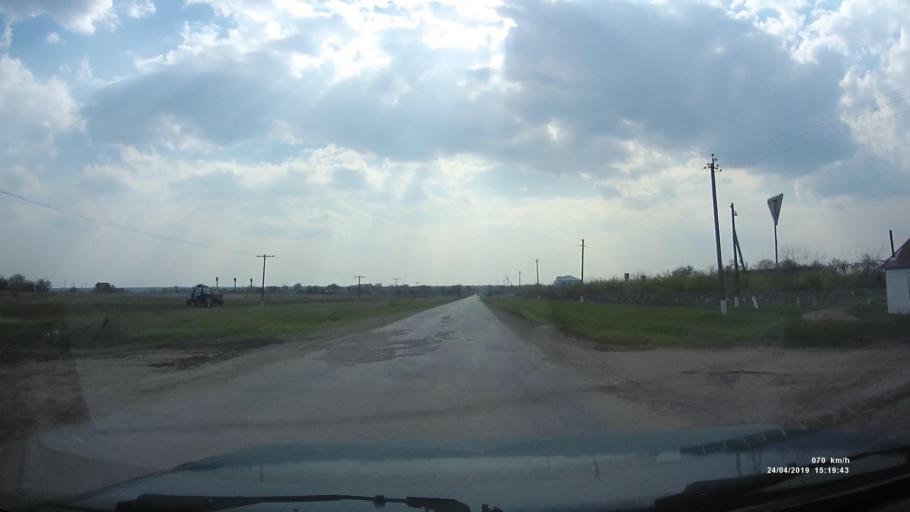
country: RU
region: Rostov
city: Remontnoye
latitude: 46.5382
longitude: 43.1417
